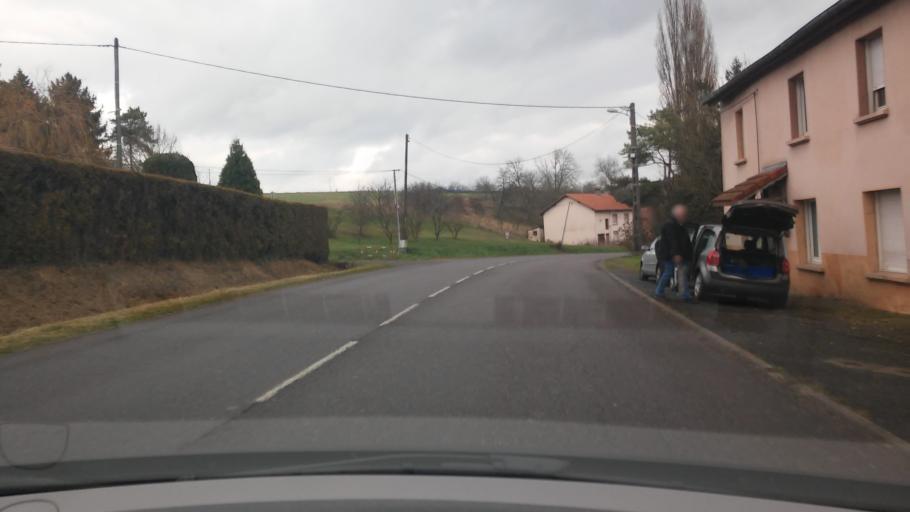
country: FR
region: Lorraine
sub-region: Departement de la Moselle
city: Crehange
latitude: 49.1080
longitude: 6.5293
